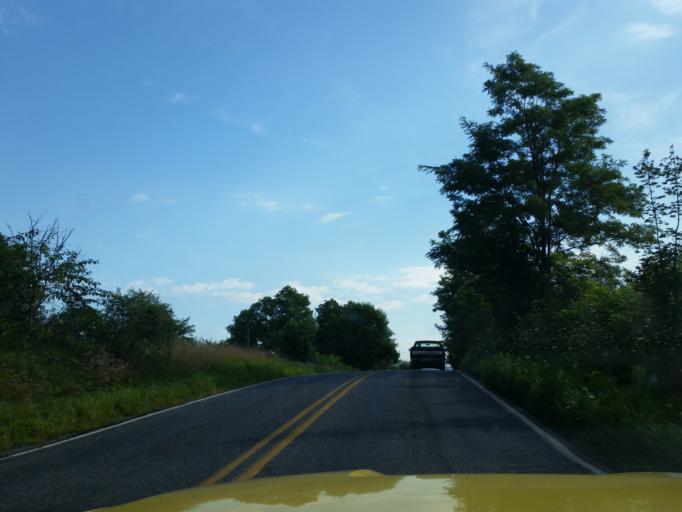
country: US
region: Pennsylvania
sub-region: Lebanon County
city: Fredericksburg
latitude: 40.4557
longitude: -76.4131
